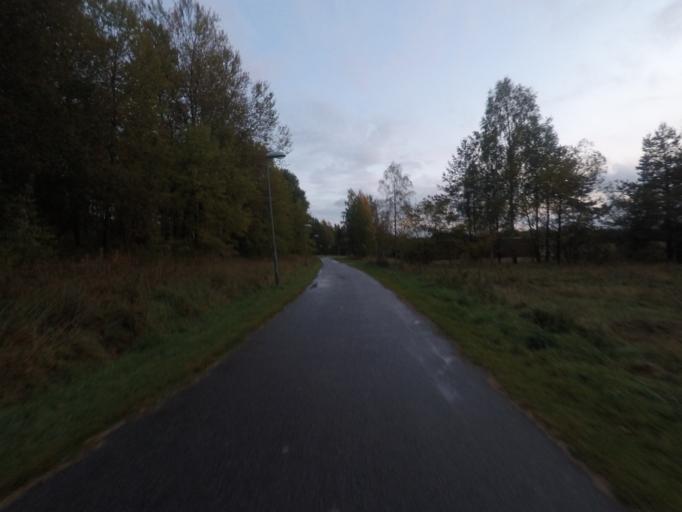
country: SE
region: OErebro
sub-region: Karlskoga Kommun
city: Karlskoga
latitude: 59.3120
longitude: 14.4865
